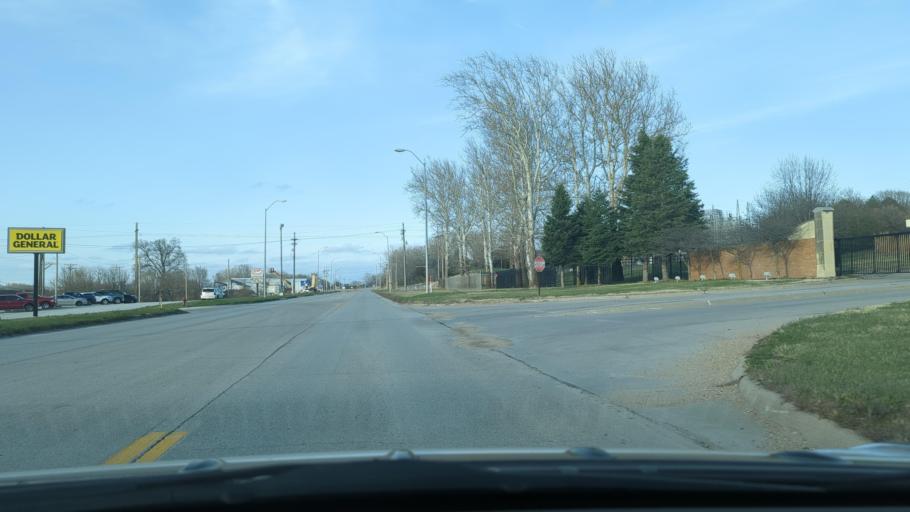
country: US
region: Nebraska
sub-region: Saunders County
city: Ashland
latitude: 41.0398
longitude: -96.3558
